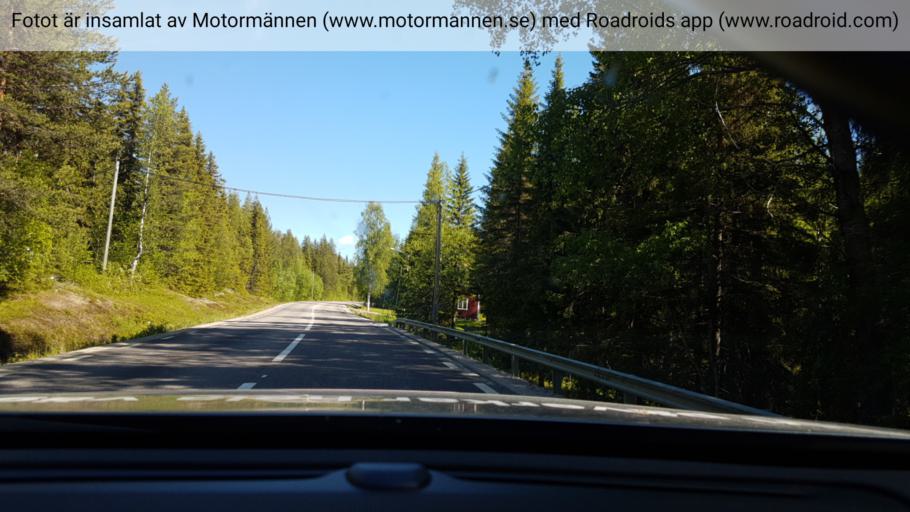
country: SE
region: Vaesterbotten
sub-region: Lycksele Kommun
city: Soderfors
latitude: 64.7118
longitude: 17.7002
